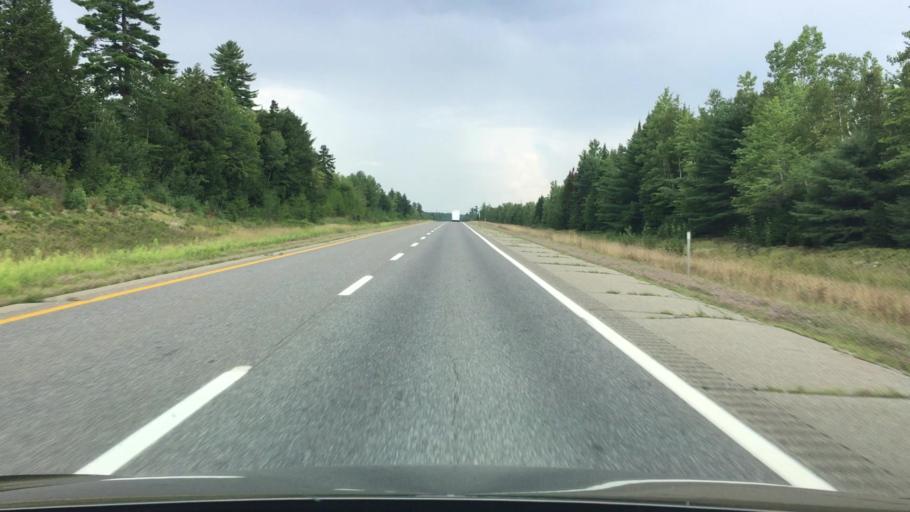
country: US
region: Maine
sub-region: Penobscot County
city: Medway
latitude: 45.5185
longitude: -68.5524
